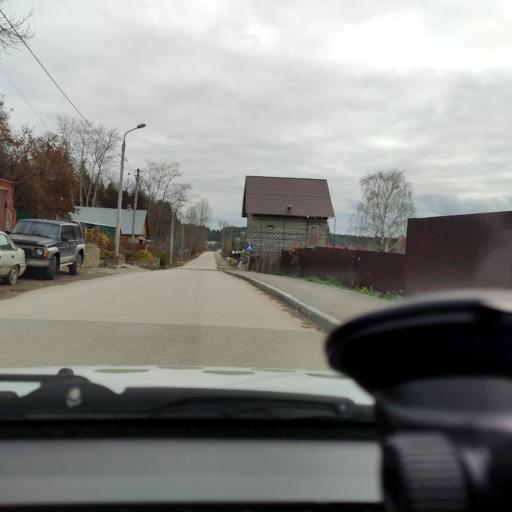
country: RU
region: Perm
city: Kondratovo
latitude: 58.0451
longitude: 56.1096
